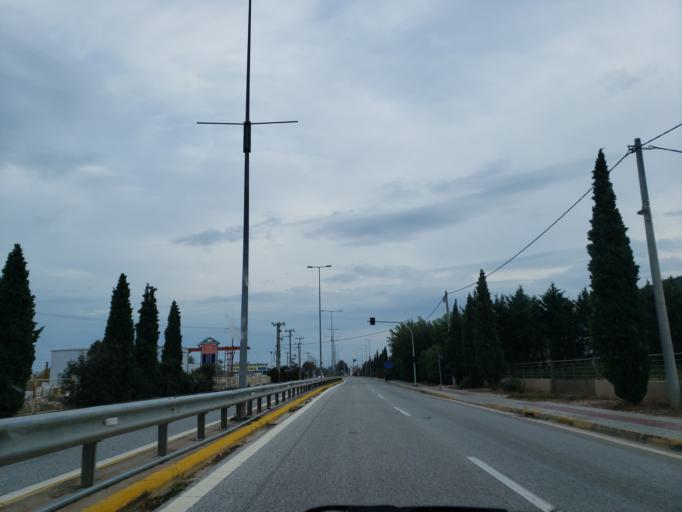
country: GR
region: Attica
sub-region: Nomarchia Anatolikis Attikis
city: Marathonas
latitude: 38.1462
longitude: 23.9649
